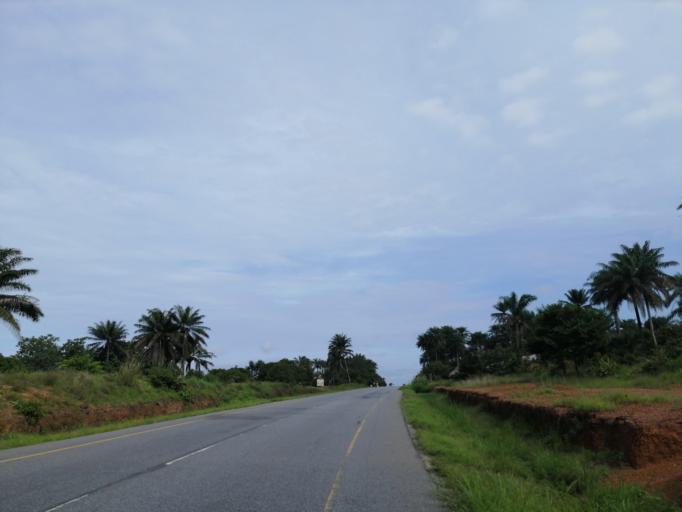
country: SL
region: Northern Province
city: Port Loko
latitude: 8.7665
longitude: -12.8887
